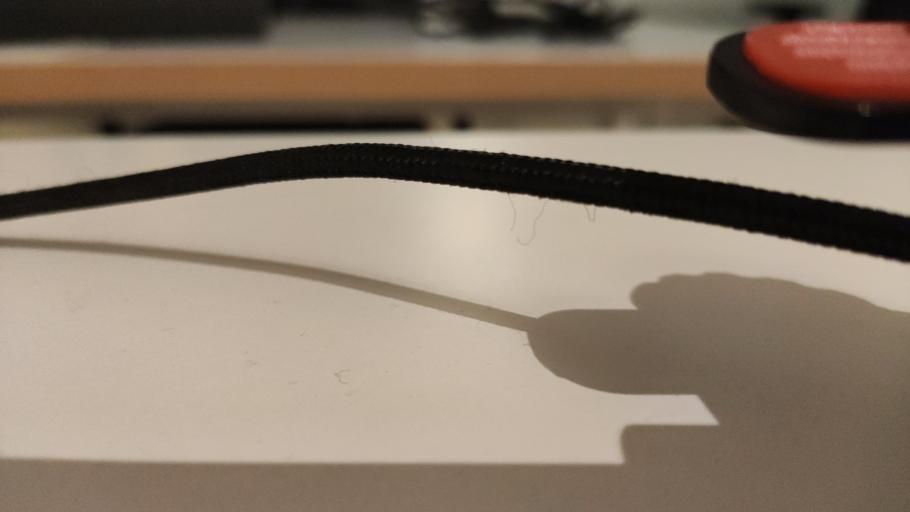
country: RU
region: Moskovskaya
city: Orekhovo-Zuyevo
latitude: 55.7807
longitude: 38.9642
